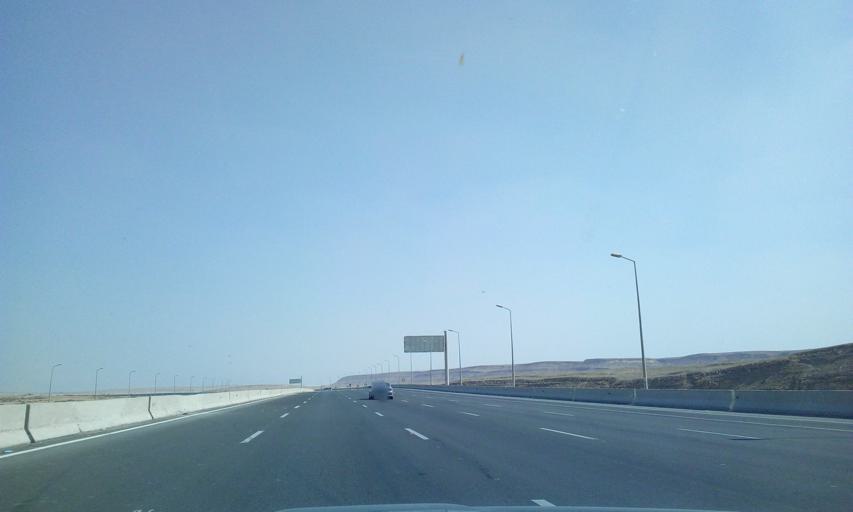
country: EG
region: As Suways
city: Ain Sukhna
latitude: 29.7876
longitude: 31.9016
